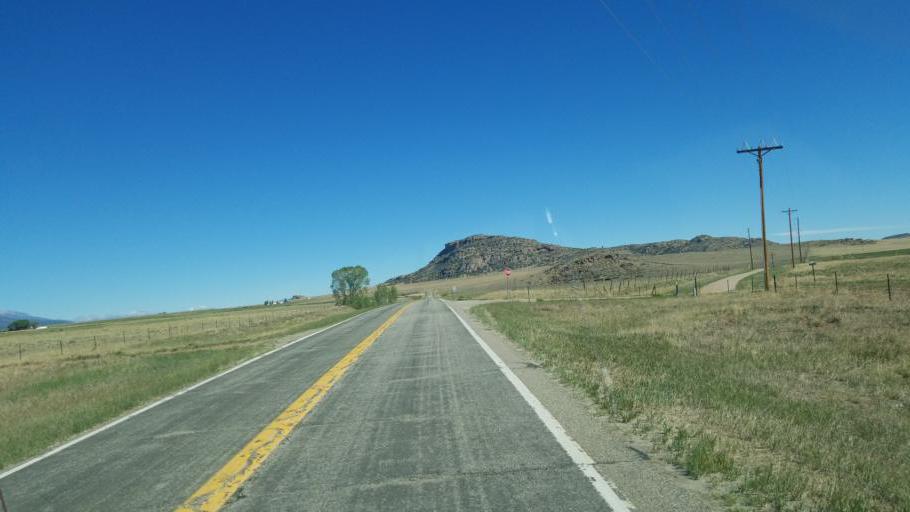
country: US
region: Colorado
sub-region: Custer County
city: Westcliffe
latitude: 38.1725
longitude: -105.5032
